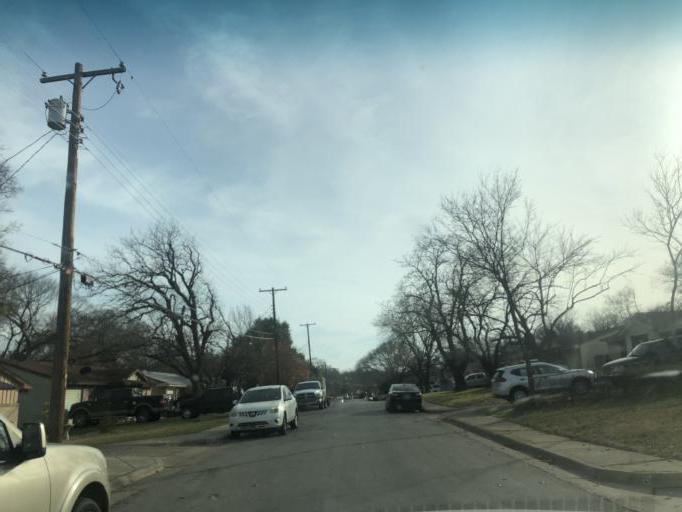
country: US
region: Texas
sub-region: Dallas County
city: Duncanville
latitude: 32.6716
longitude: -96.8963
